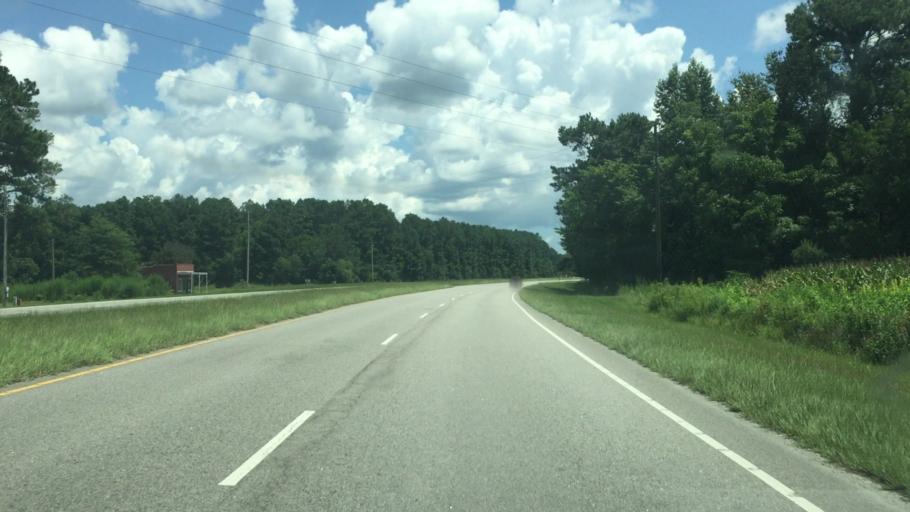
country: US
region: South Carolina
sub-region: Horry County
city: Loris
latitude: 34.0080
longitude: -78.7657
